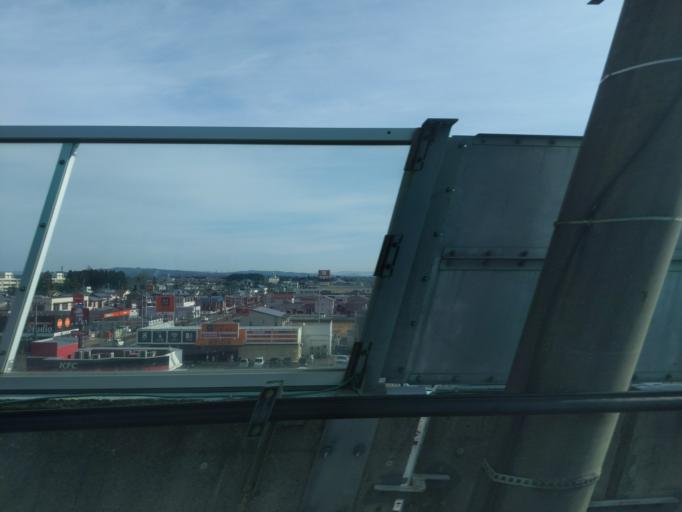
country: JP
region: Miyagi
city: Furukawa
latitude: 38.5752
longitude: 140.9690
